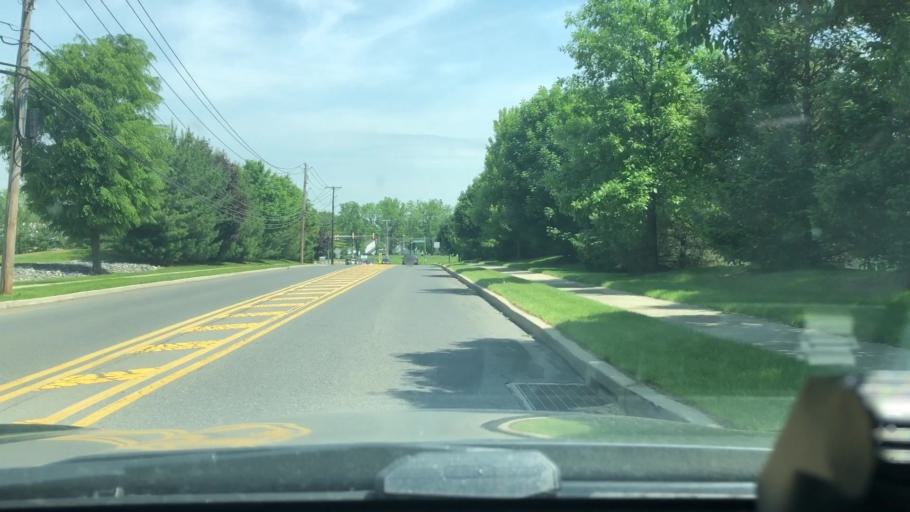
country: US
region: Pennsylvania
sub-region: Northampton County
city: Bethlehem
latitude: 40.6585
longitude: -75.3973
